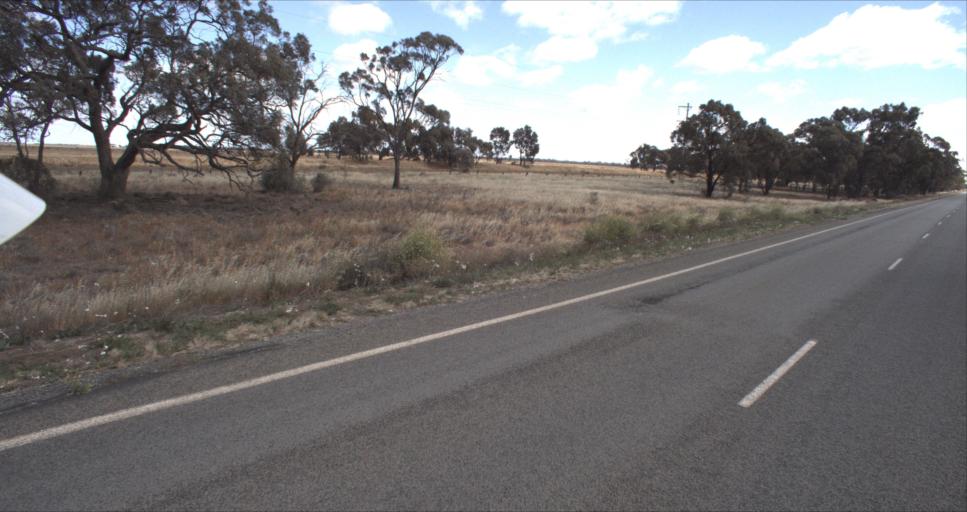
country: AU
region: New South Wales
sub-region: Murrumbidgee Shire
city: Darlington Point
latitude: -34.5686
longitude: 146.1676
